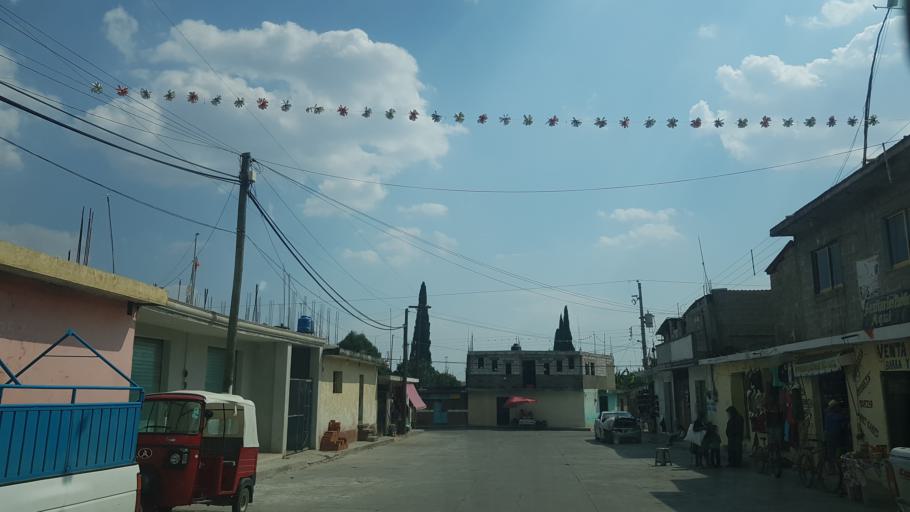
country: MX
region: Puebla
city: San Juan Amecac
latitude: 18.8342
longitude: -98.6596
